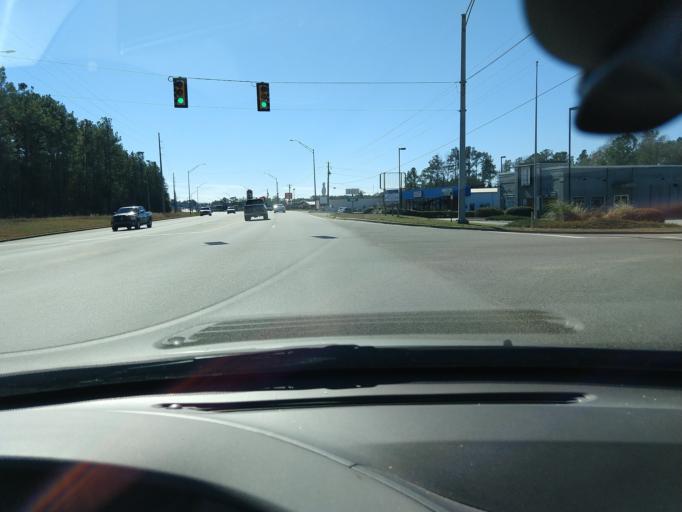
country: US
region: Alabama
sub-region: Covington County
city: Andalusia
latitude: 31.3136
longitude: -86.4992
